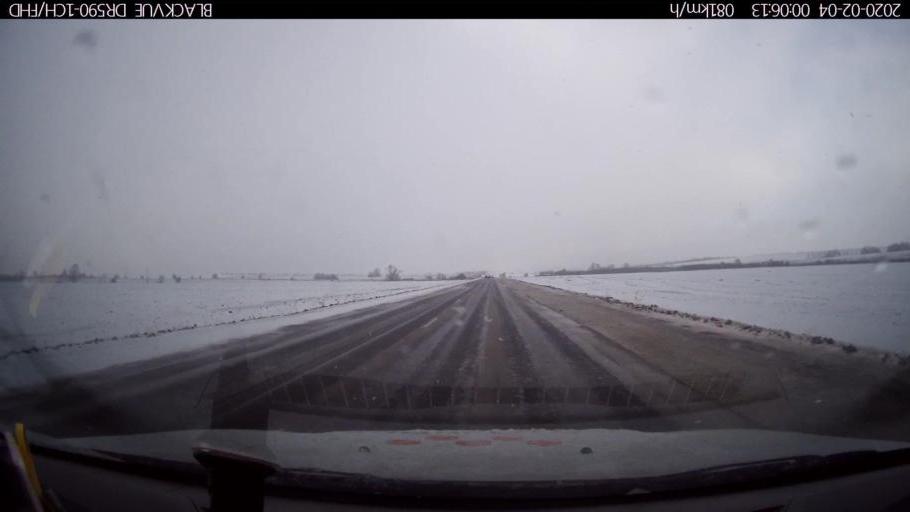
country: RU
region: Nizjnij Novgorod
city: Dal'neye Konstantinovo
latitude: 55.8454
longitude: 44.1274
